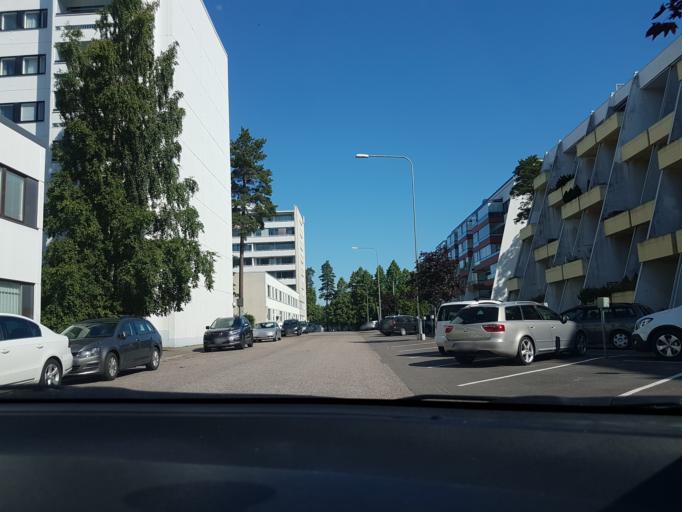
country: FI
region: Uusimaa
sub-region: Helsinki
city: Vantaa
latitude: 60.2110
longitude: 25.1376
